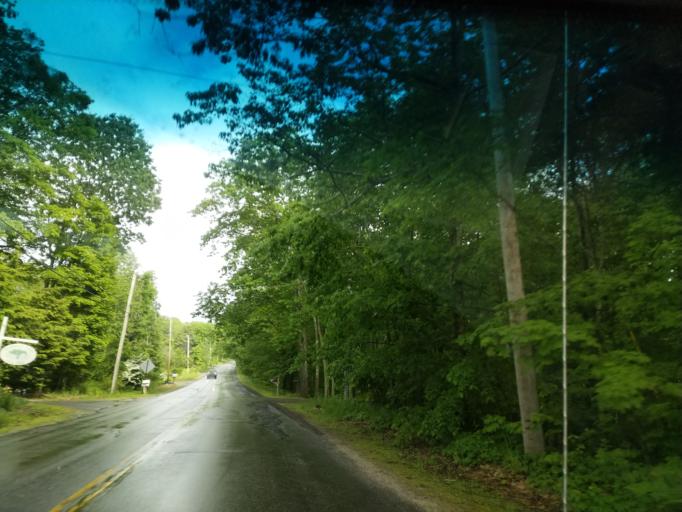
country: US
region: Maine
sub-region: Cumberland County
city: Cumberland Center
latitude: 43.7872
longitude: -70.3484
